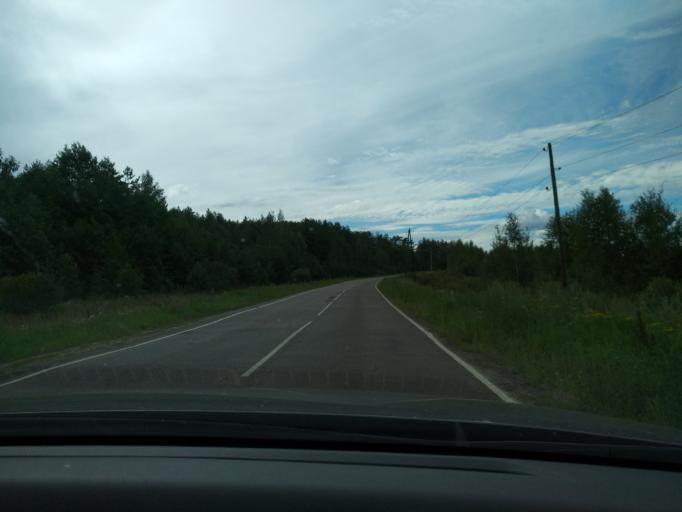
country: RU
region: Moskovskaya
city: Krasnyy Tkach
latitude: 55.3810
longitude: 39.1929
